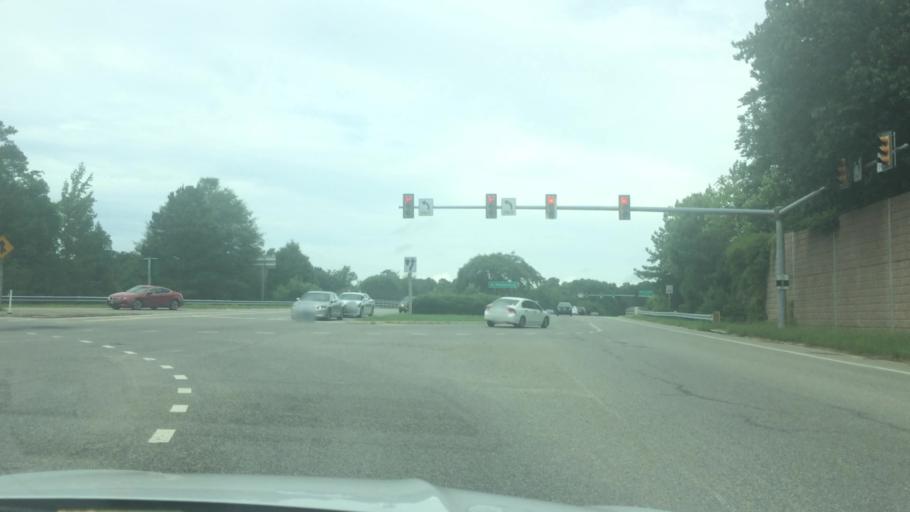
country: US
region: Virginia
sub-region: James City County
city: Williamsburg
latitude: 37.2987
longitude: -76.7439
